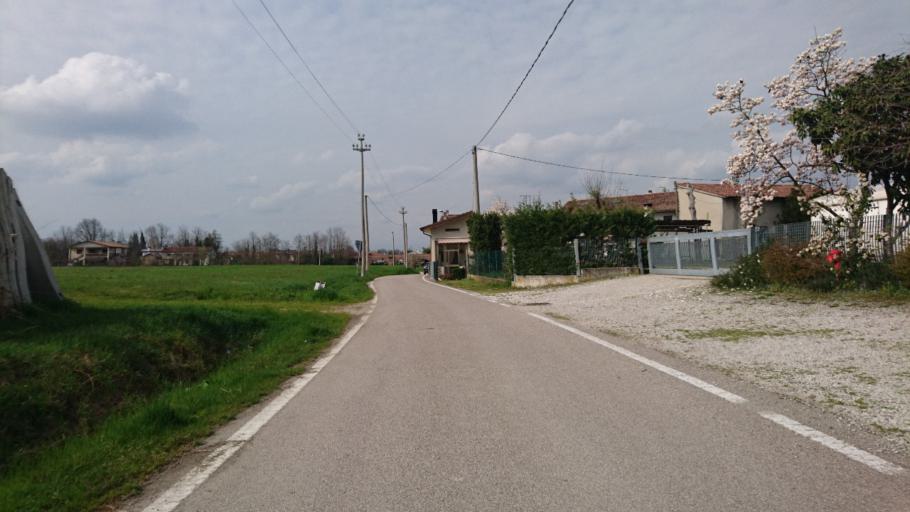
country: IT
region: Veneto
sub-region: Provincia di Padova
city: Piazzola sul Brenta
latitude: 45.5334
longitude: 11.7947
